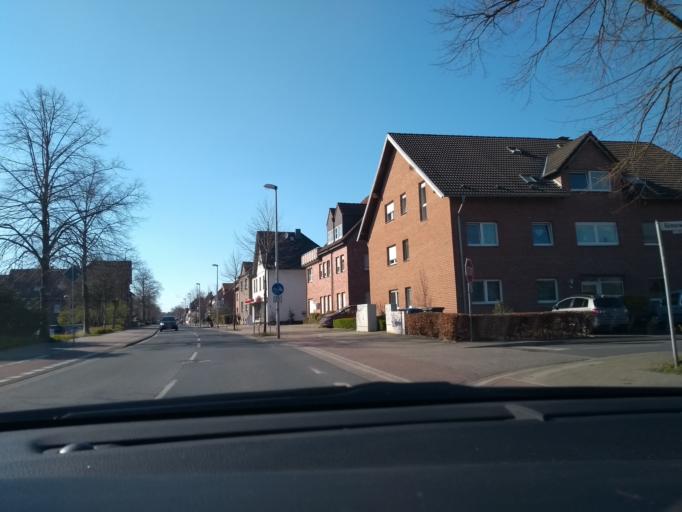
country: DE
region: North Rhine-Westphalia
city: Lunen
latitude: 51.6273
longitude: 7.4946
